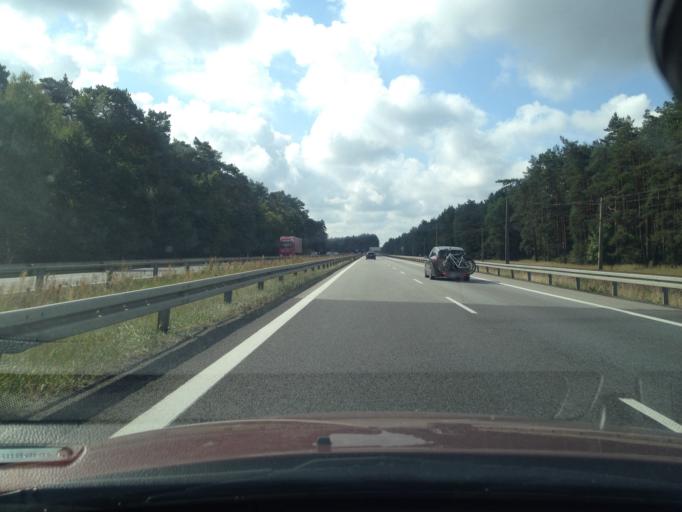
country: PL
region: West Pomeranian Voivodeship
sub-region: Powiat goleniowski
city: Goleniow
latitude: 53.4744
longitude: 14.7891
